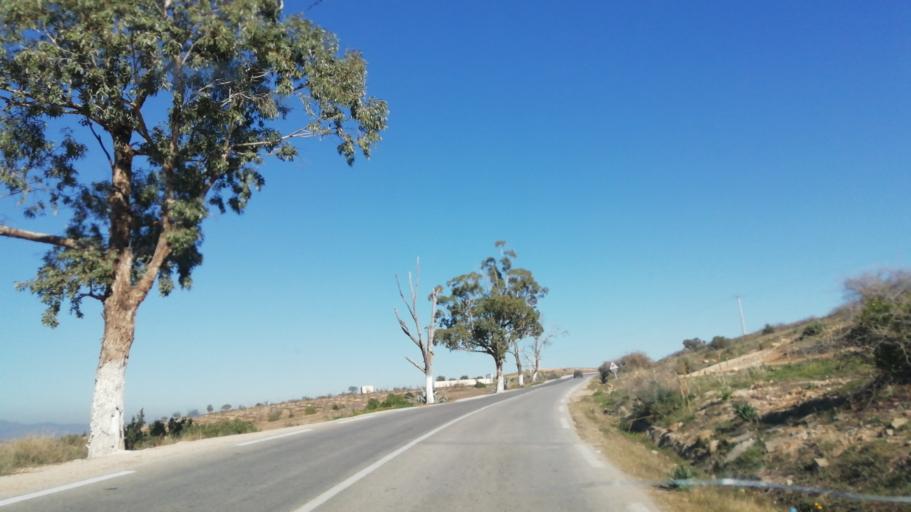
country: DZ
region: Tlemcen
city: Nedroma
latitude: 34.8282
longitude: -1.6495
